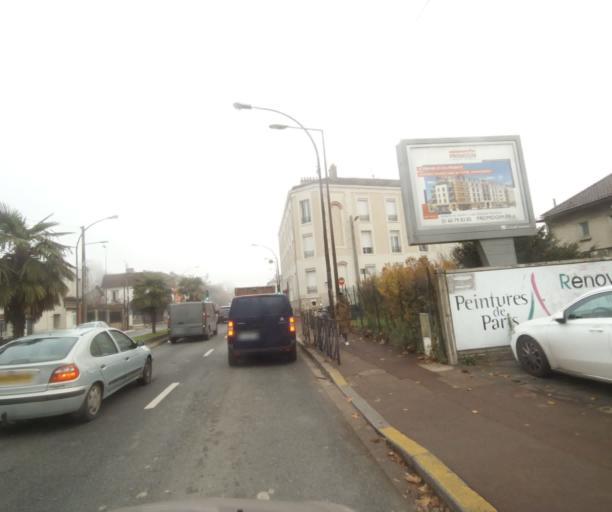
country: FR
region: Ile-de-France
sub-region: Departement de Seine-Saint-Denis
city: Livry-Gargan
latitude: 48.9158
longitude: 2.5302
